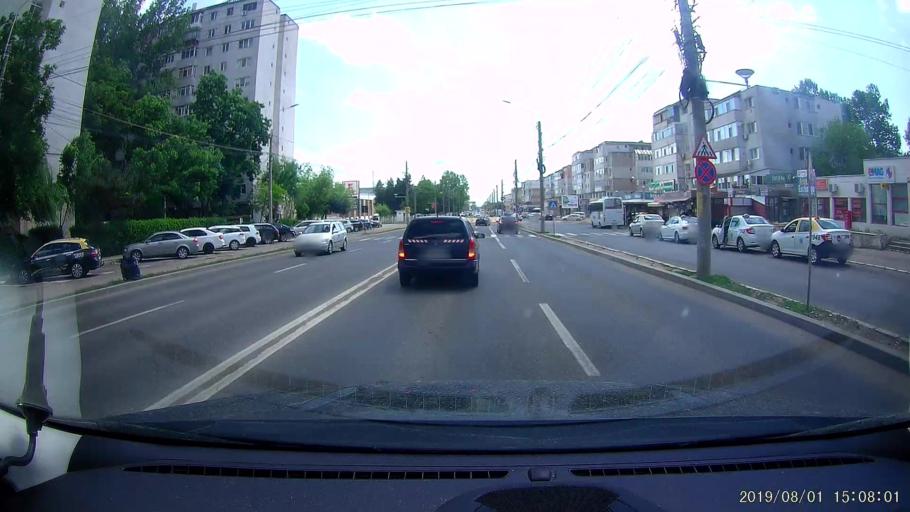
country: RO
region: Braila
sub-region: Municipiul Braila
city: Braila
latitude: 45.2438
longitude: 27.9475
